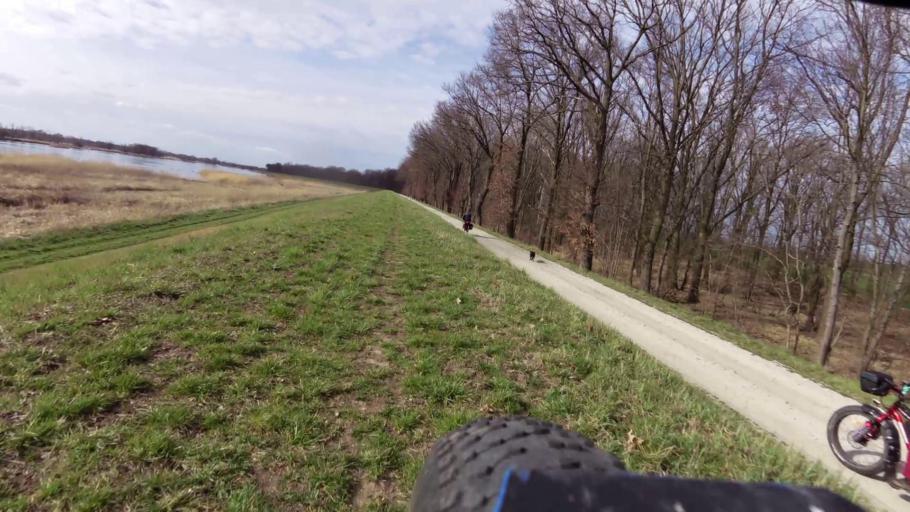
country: PL
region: Lubusz
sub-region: Powiat slubicki
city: Gorzyca
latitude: 52.5025
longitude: 14.6349
